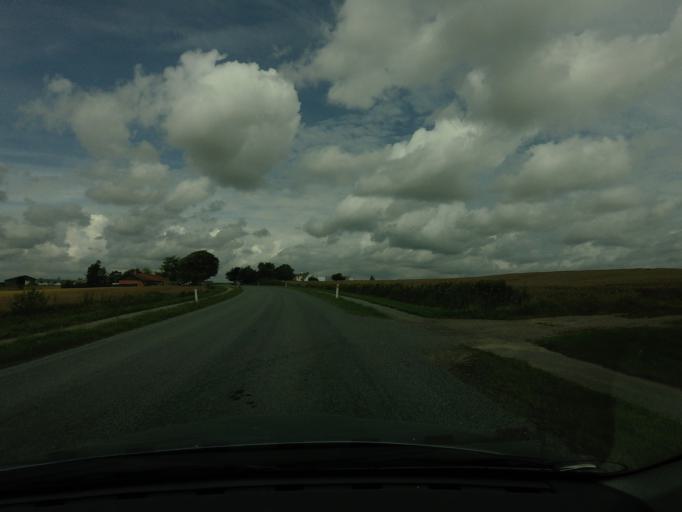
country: DK
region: North Denmark
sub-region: Hjorring Kommune
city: Tars
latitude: 57.3519
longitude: 10.2237
